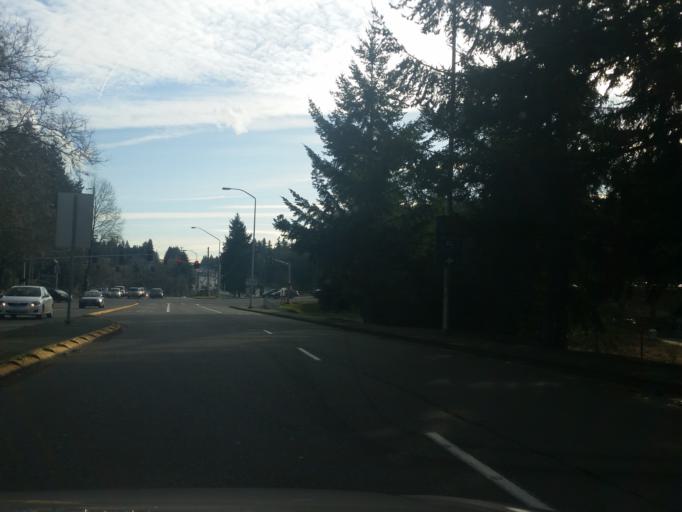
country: US
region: Washington
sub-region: King County
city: Shoreline
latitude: 47.7352
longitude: -122.3237
